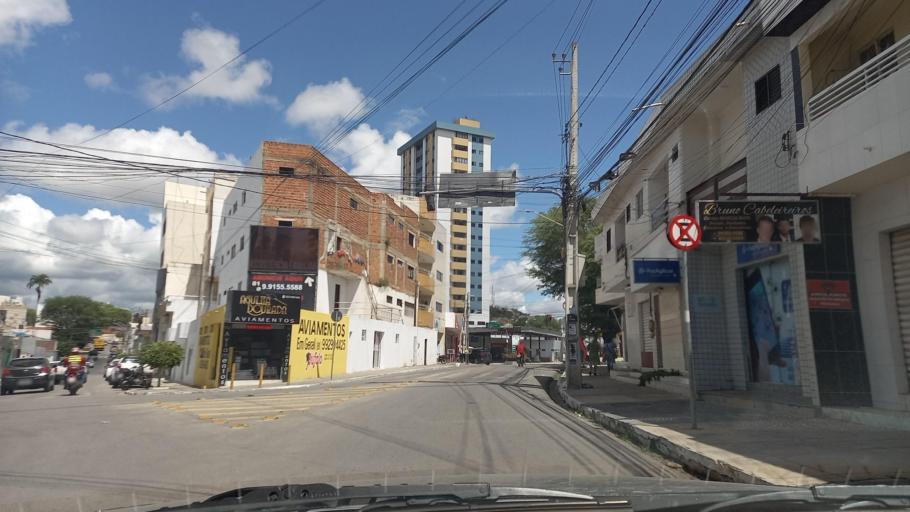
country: BR
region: Pernambuco
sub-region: Caruaru
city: Caruaru
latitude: -8.2768
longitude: -35.9672
